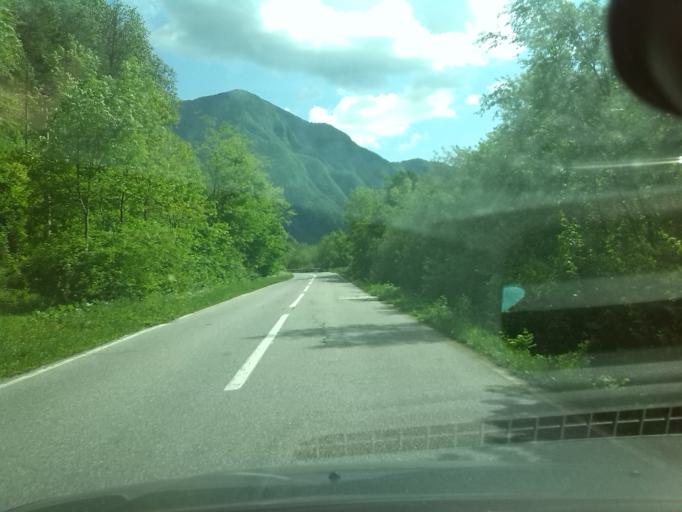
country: IT
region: Friuli Venezia Giulia
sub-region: Provincia di Udine
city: Pulfero
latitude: 46.2370
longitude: 13.5021
